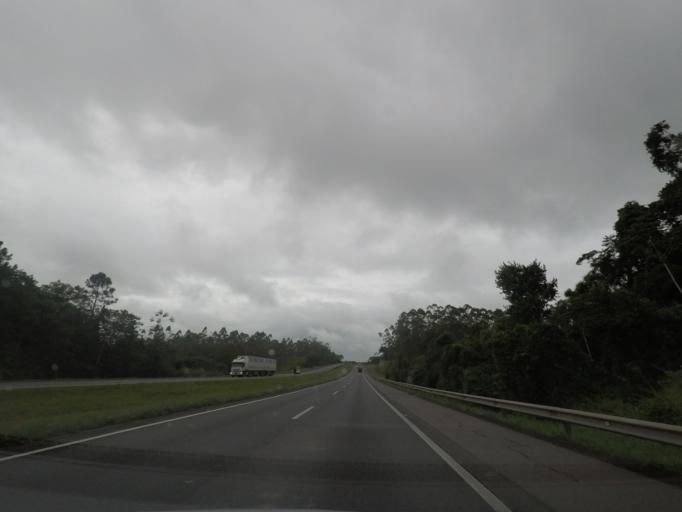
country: BR
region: Sao Paulo
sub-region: Jacupiranga
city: Jacupiranga
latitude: -24.6501
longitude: -47.9358
